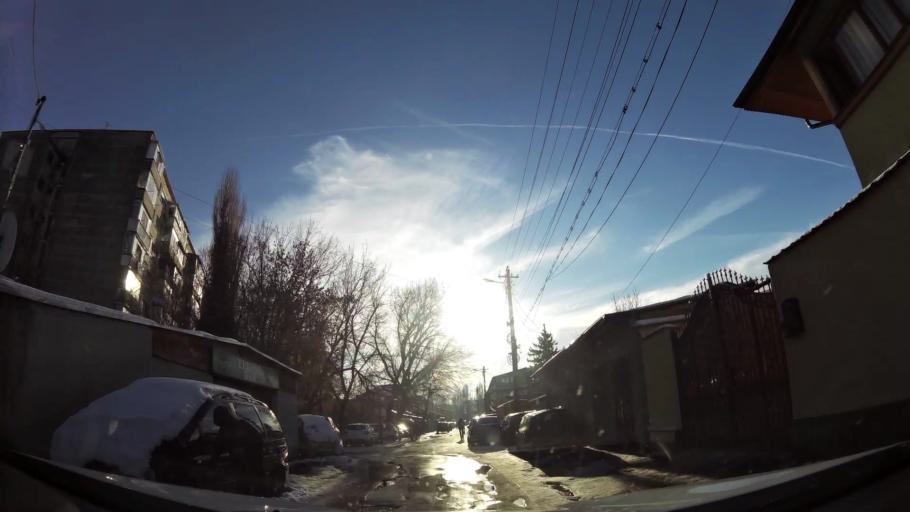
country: RO
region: Bucuresti
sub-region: Municipiul Bucuresti
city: Bucuresti
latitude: 44.3874
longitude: 26.0884
